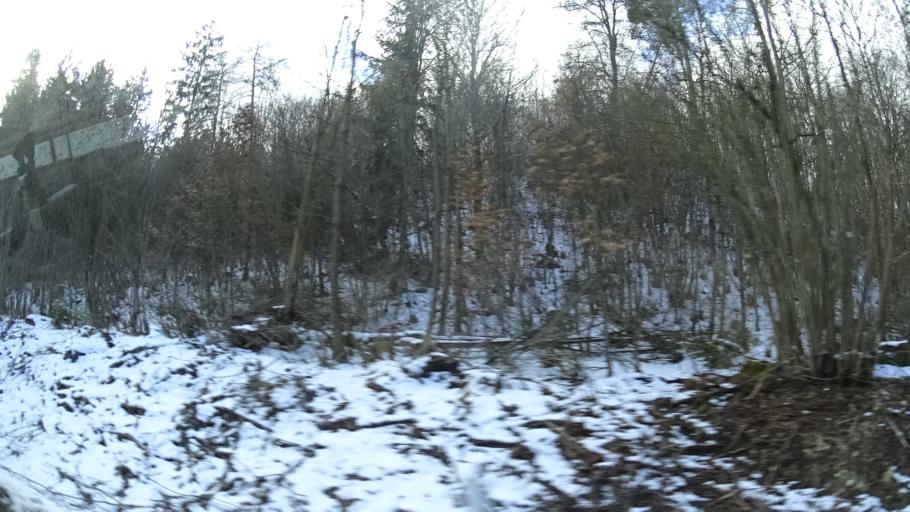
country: DE
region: Thuringia
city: Kuhndorf
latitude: 50.5951
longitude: 10.4660
